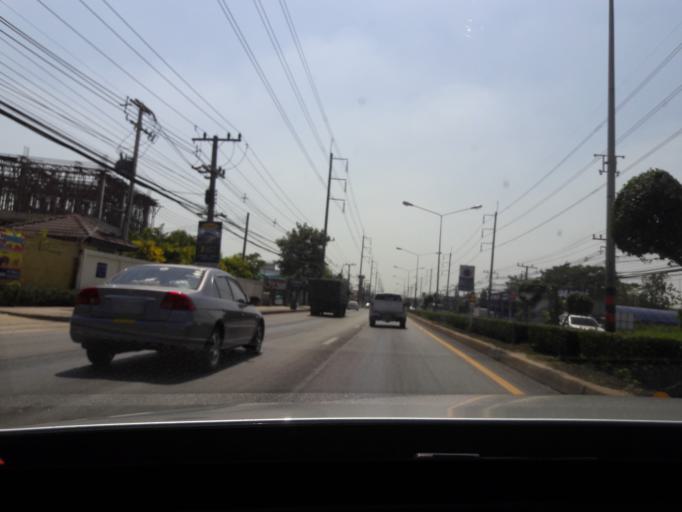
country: TH
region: Samut Sakhon
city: Krathum Baen
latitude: 13.6323
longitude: 100.2956
